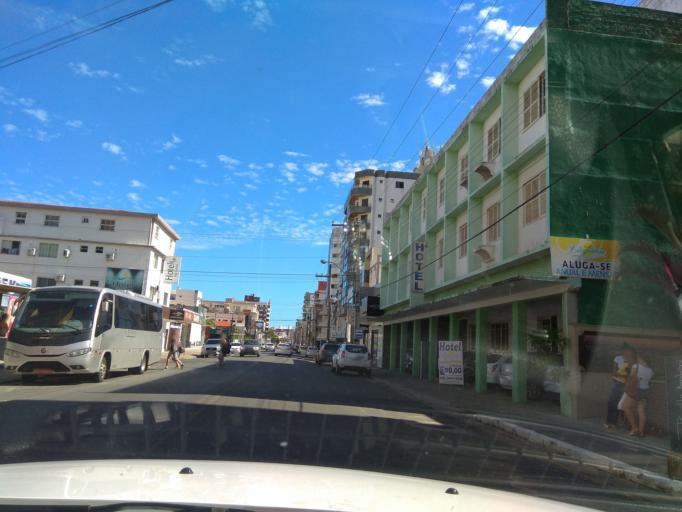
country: BR
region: Santa Catarina
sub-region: Laguna
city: Laguna
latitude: -28.4792
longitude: -48.7690
